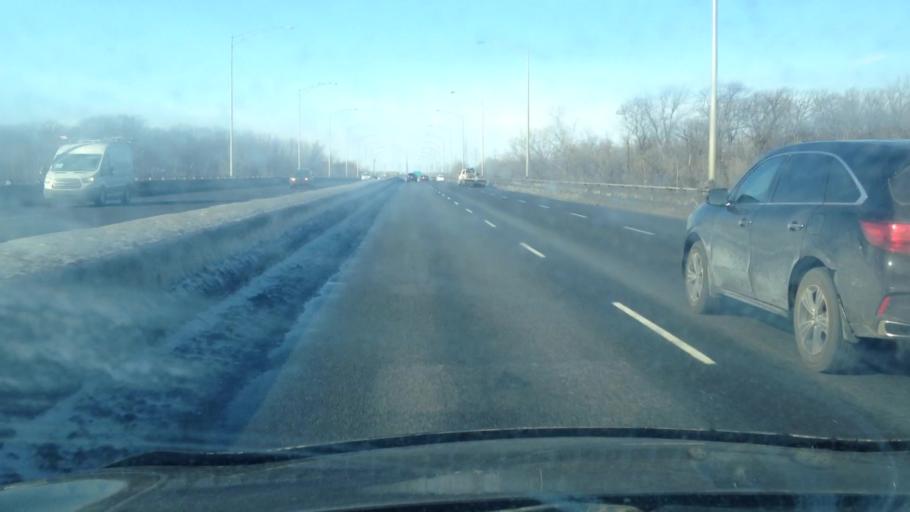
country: CA
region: Quebec
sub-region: Laurentides
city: Boisbriand
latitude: 45.5787
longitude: -73.8354
